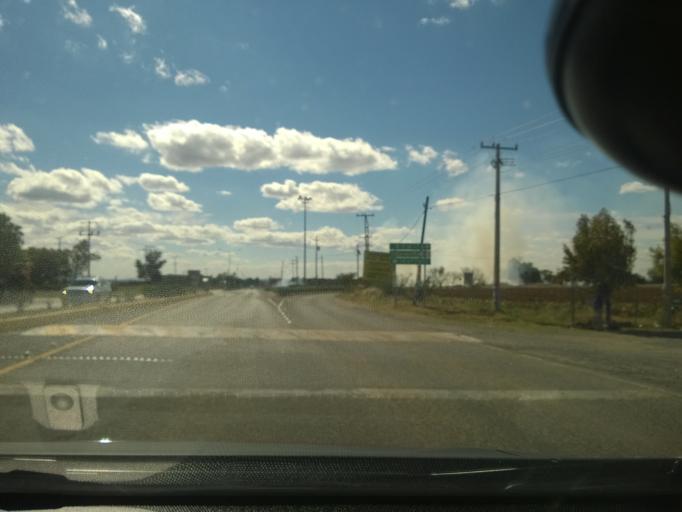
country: MX
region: Guanajuato
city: Romita
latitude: 20.8786
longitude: -101.5041
